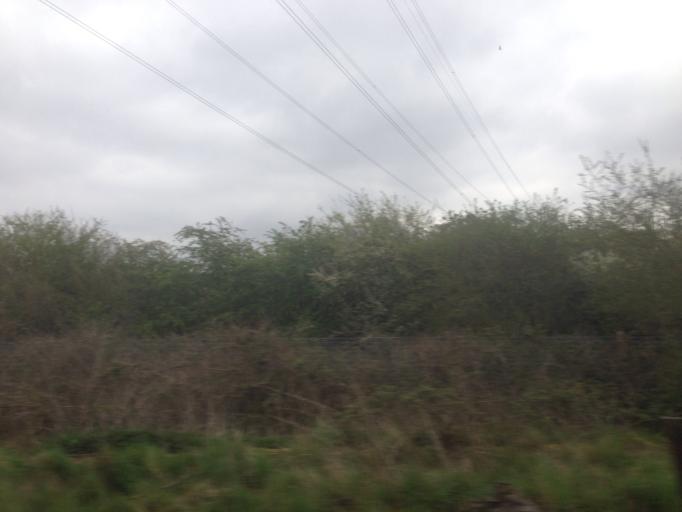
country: GB
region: England
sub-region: Greater London
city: Mitcham
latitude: 51.3866
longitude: -0.1528
